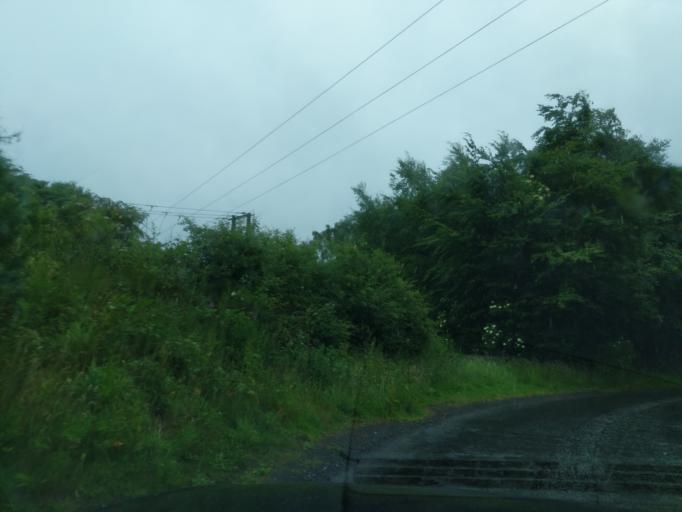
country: GB
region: Scotland
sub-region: Midlothian
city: Loanhead
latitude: 55.8531
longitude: -3.1772
